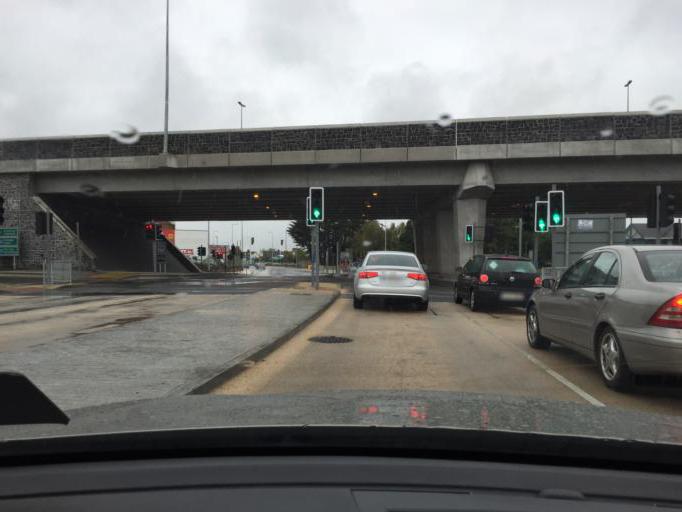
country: IE
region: Leinster
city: Clondalkin
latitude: 53.3124
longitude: -6.3902
